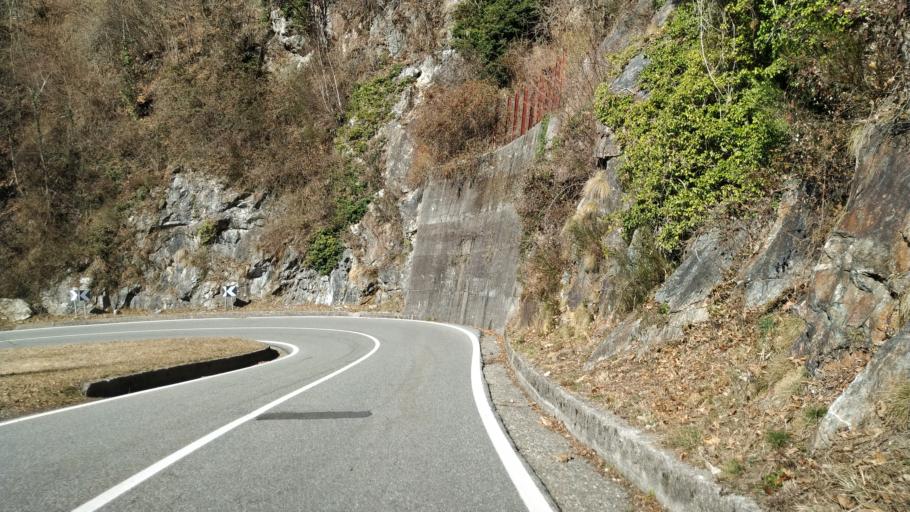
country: IT
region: Piedmont
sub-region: Provincia di Vercelli
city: Civiasco
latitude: 45.8037
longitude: 8.2857
